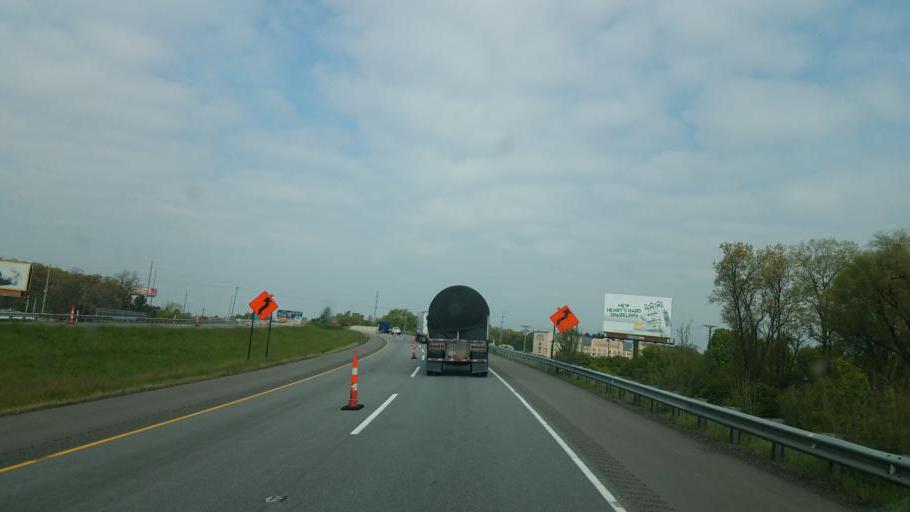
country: US
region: Indiana
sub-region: Saint Joseph County
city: Georgetown
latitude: 41.7220
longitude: -86.2476
